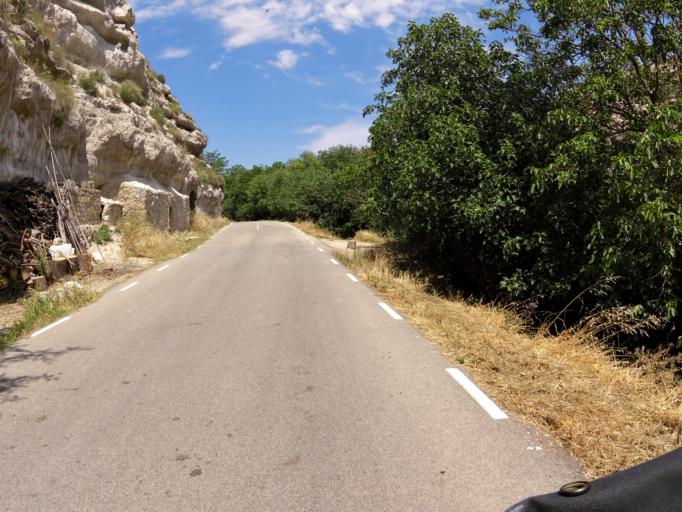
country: ES
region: Castille-La Mancha
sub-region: Provincia de Albacete
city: Jorquera
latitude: 39.1652
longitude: -1.5455
